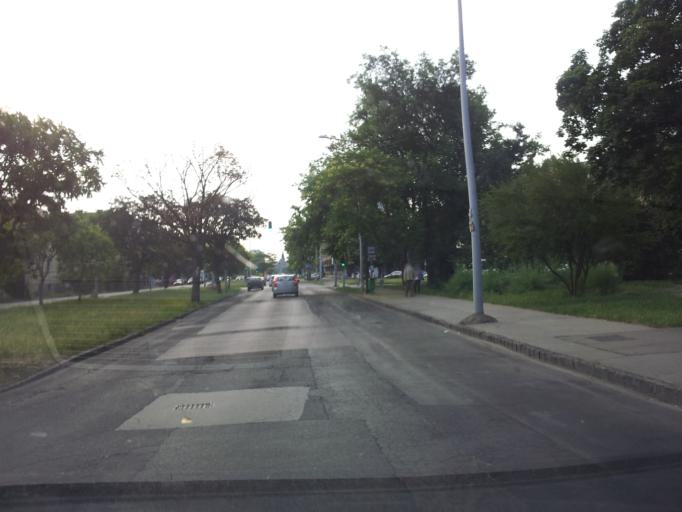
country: HU
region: Budapest
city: Budapest XI. keruelet
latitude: 47.4769
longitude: 19.0336
